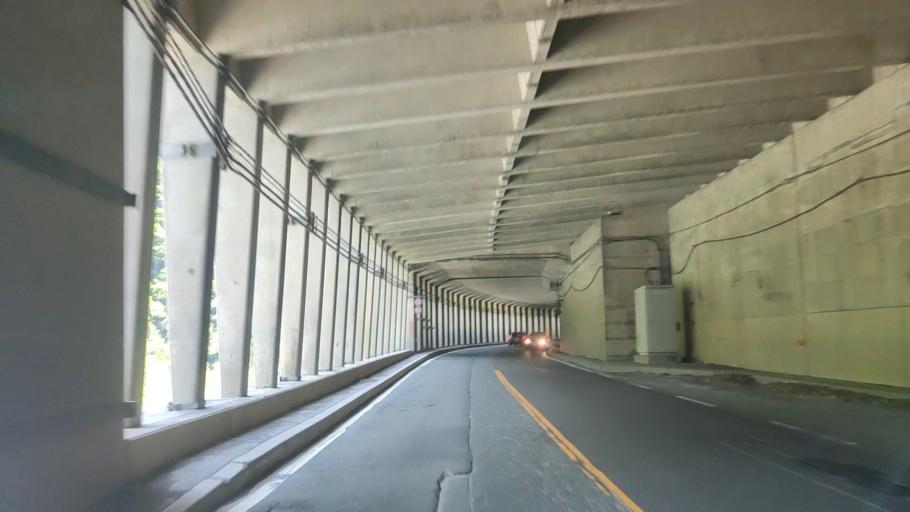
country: JP
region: Niigata
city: Itoigawa
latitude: 36.9110
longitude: 137.8631
